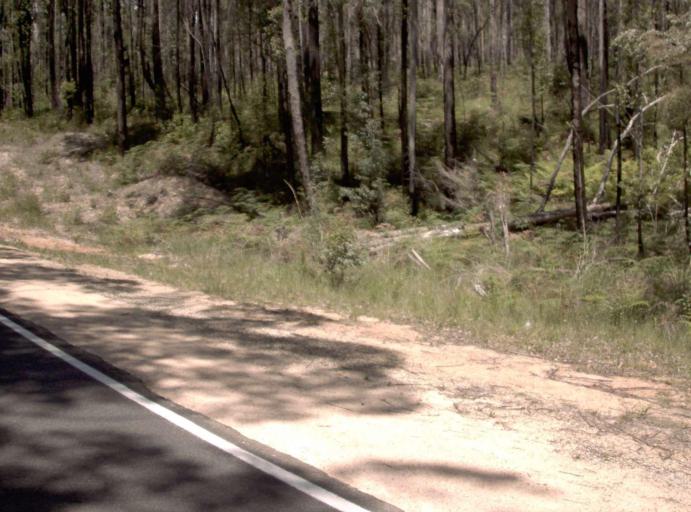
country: AU
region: New South Wales
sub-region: Bombala
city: Bombala
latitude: -37.6348
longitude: 148.8685
